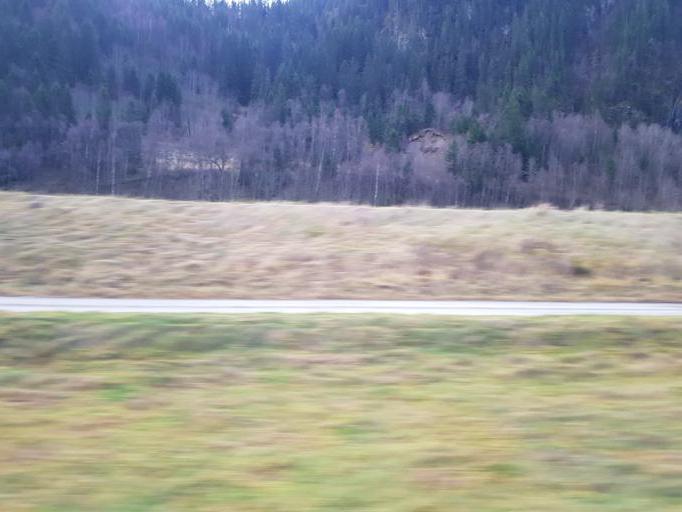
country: NO
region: Sor-Trondelag
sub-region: Midtre Gauldal
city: Storen
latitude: 63.0694
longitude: 10.2727
